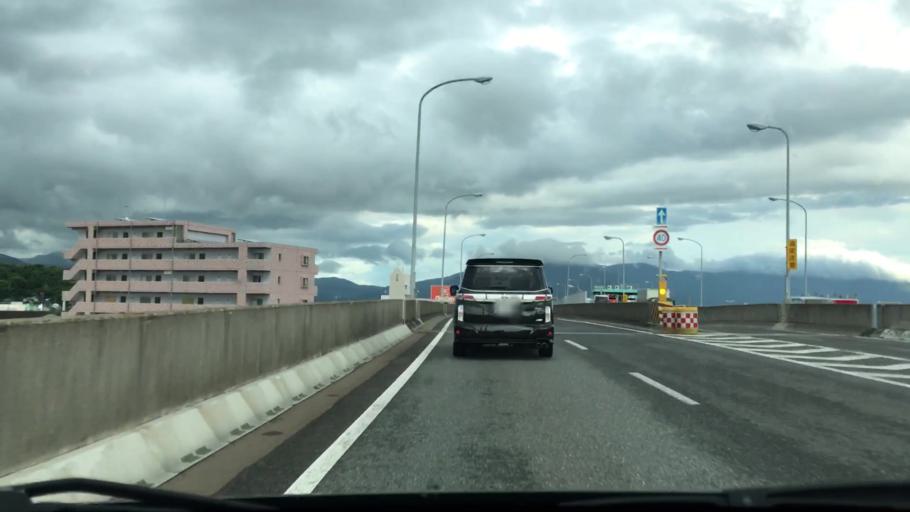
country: JP
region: Fukuoka
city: Fukuoka-shi
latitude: 33.6321
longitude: 130.4334
